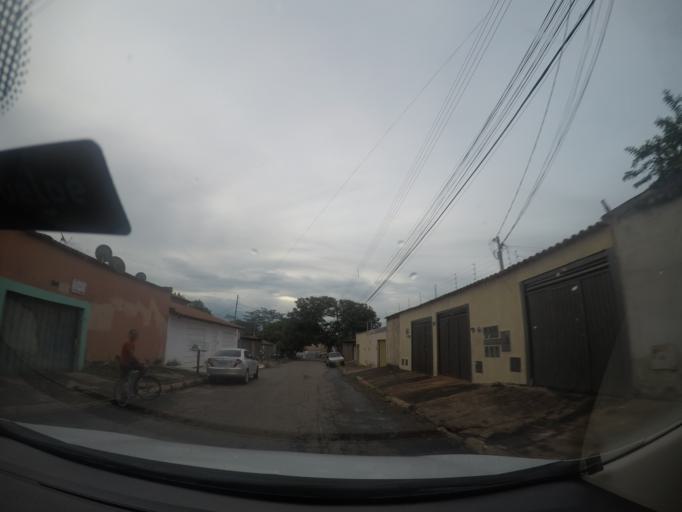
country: BR
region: Goias
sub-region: Goiania
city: Goiania
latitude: -16.6322
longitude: -49.2387
